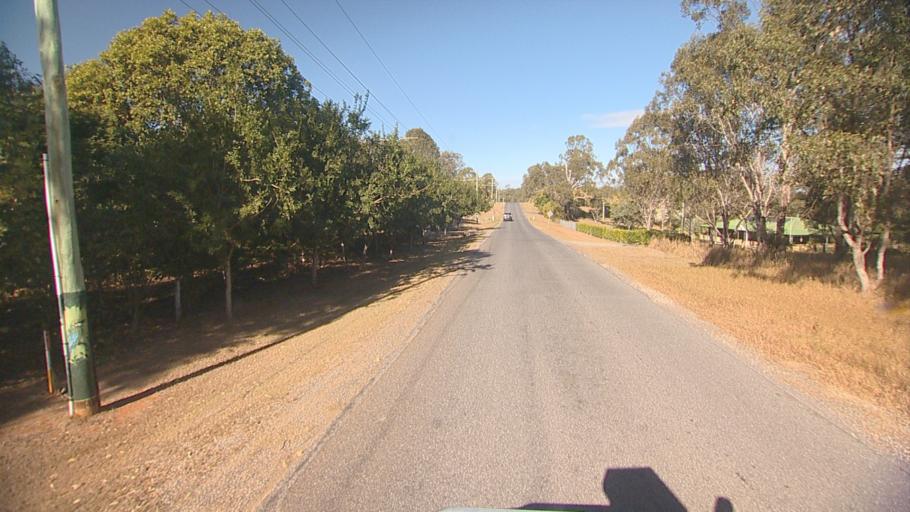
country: AU
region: Queensland
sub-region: Logan
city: Cedar Vale
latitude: -27.8631
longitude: 152.9851
